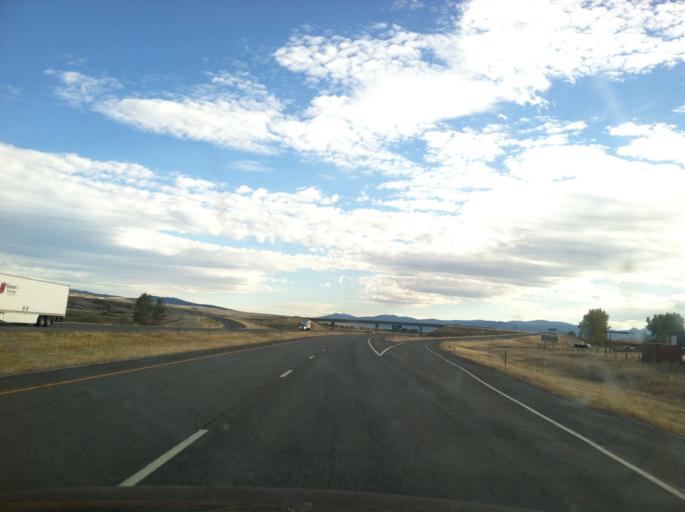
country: US
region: Montana
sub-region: Deer Lodge County
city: Warm Springs
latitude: 46.2740
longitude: -112.7475
